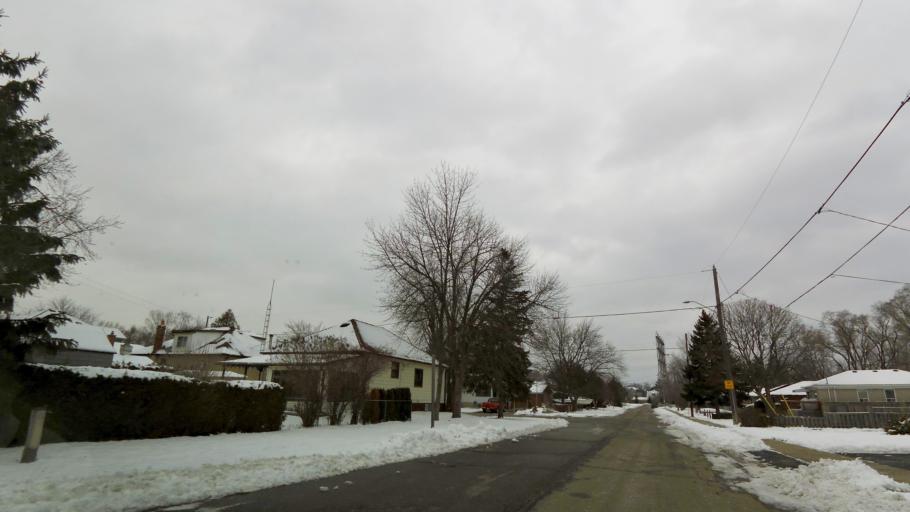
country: CA
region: Ontario
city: Etobicoke
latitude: 43.5798
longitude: -79.5621
